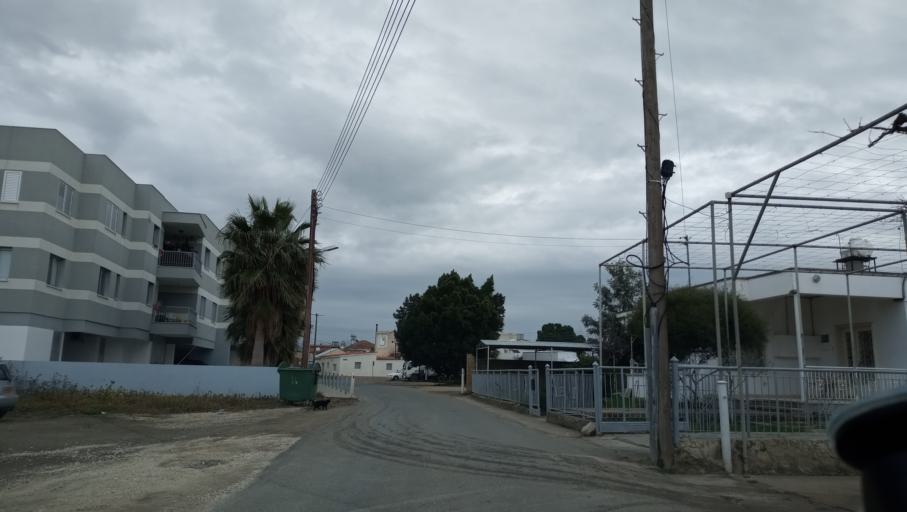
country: CY
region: Lefkosia
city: Pano Deftera
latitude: 35.0820
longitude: 33.2699
